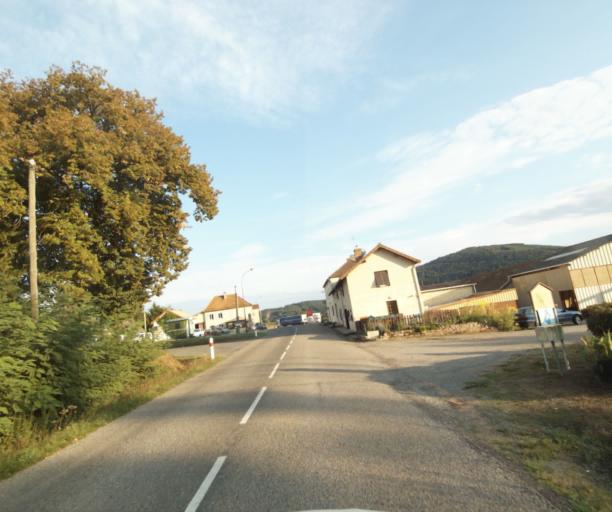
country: FR
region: Bourgogne
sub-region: Departement de Saone-et-Loire
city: Charolles
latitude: 46.4289
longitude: 4.4079
